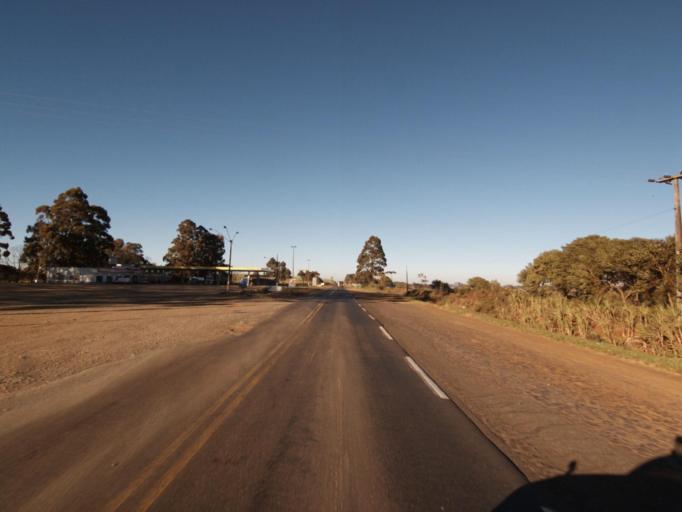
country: AR
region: Misiones
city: Bernardo de Irigoyen
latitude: -26.3105
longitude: -53.5471
